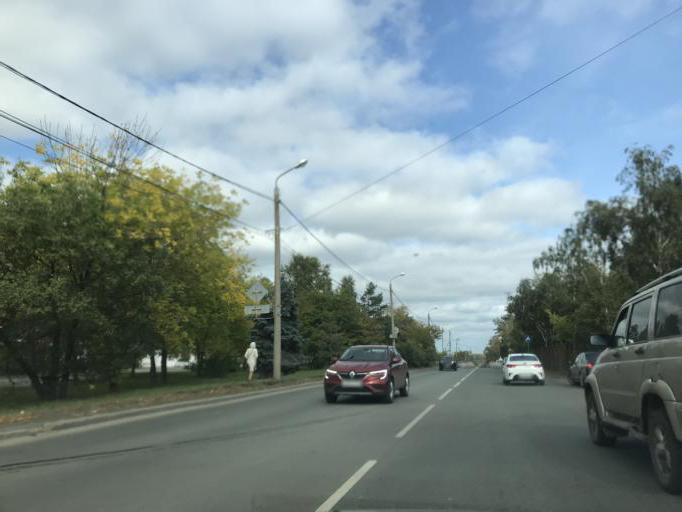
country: RU
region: Chelyabinsk
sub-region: Gorod Chelyabinsk
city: Chelyabinsk
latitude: 55.1936
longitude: 61.3631
